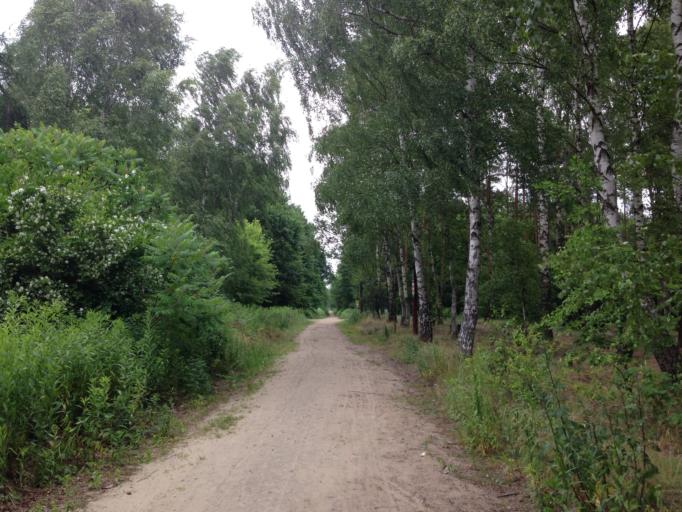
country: PL
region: Masovian Voivodeship
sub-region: Powiat warszawski zachodni
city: Babice
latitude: 52.2531
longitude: 20.8669
